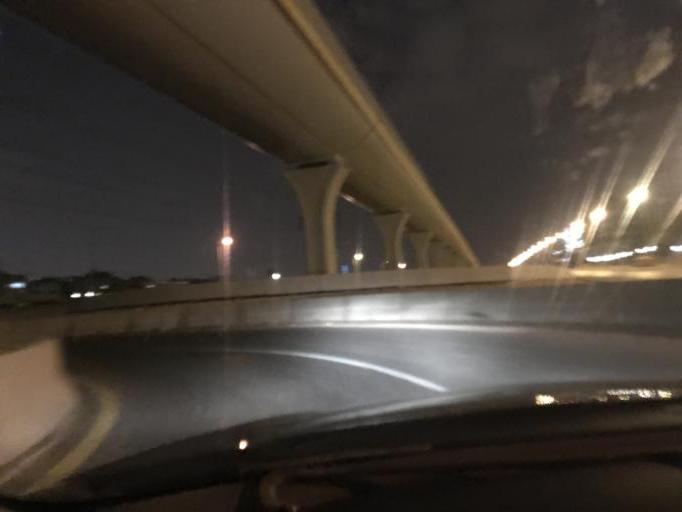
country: SA
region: Ar Riyad
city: Riyadh
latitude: 24.7986
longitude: 46.6889
